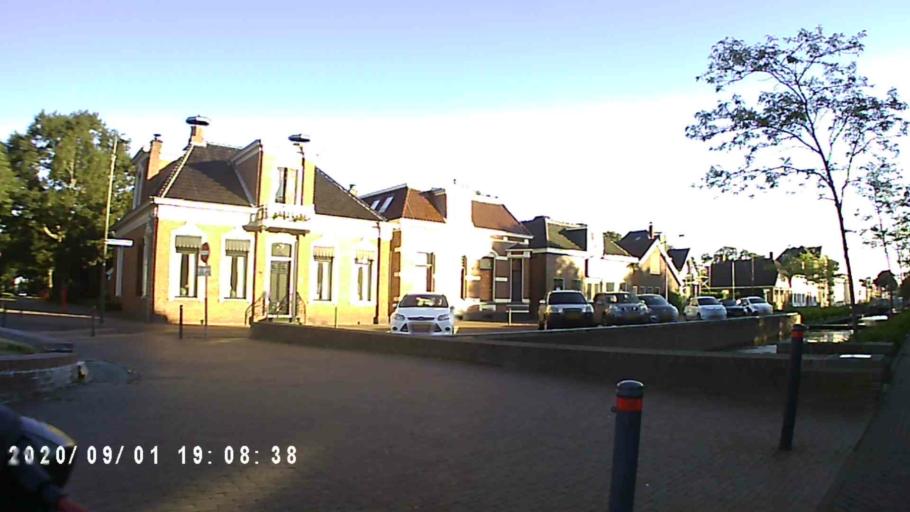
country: NL
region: Groningen
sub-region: Gemeente Veendam
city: Veendam
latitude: 53.1057
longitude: 6.8815
